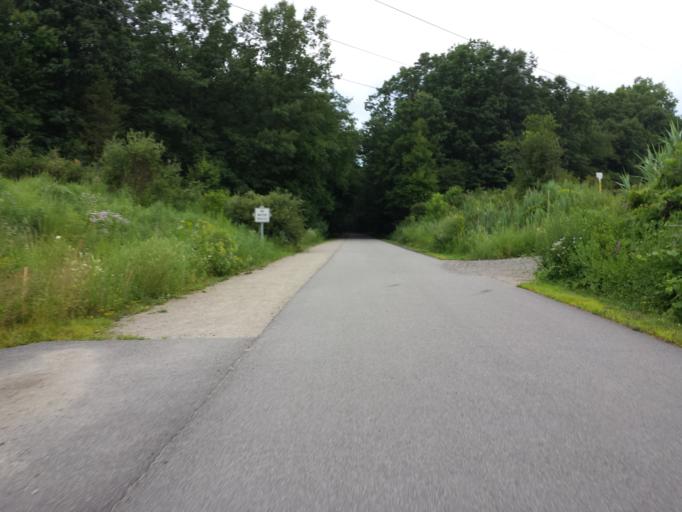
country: US
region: New York
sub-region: Dutchess County
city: Myers Corner
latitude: 41.6138
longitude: -73.8440
